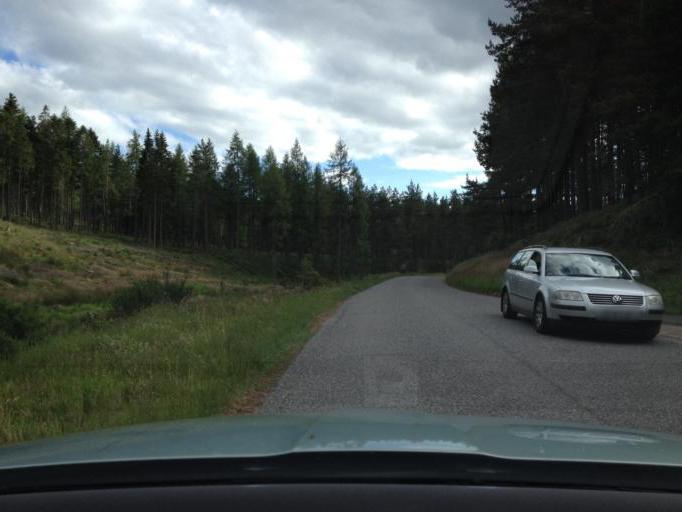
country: GB
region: Scotland
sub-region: Aberdeenshire
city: Banchory
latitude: 56.9977
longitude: -2.5725
